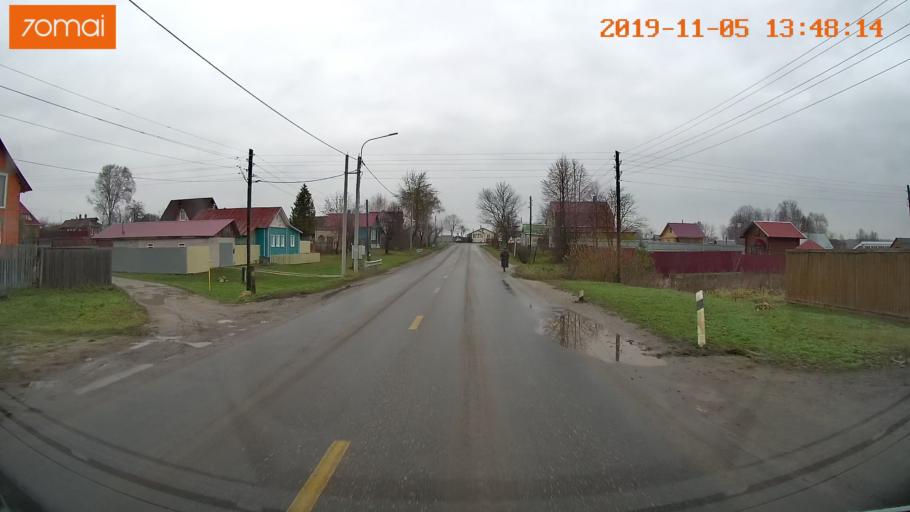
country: RU
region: Ivanovo
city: Shuya
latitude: 57.0028
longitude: 41.4052
